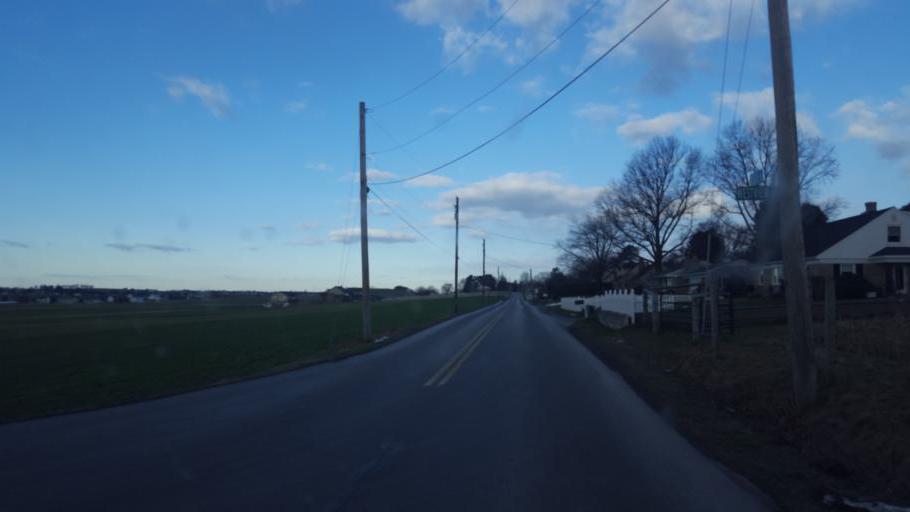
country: US
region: Pennsylvania
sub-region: Lancaster County
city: Intercourse
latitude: 40.0530
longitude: -76.0934
